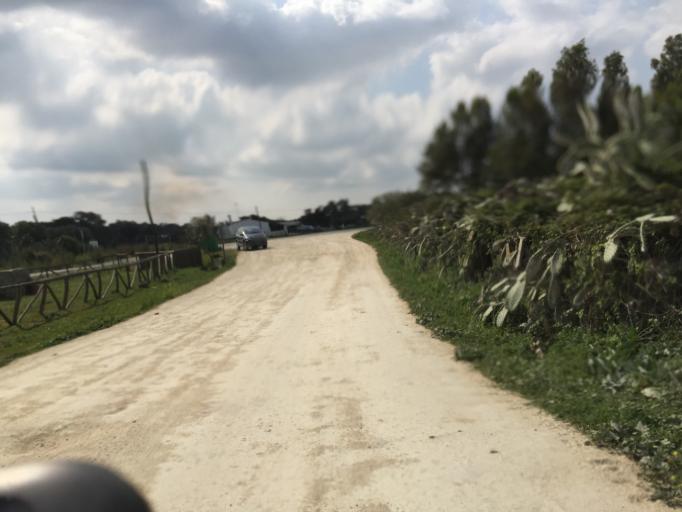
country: ES
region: Andalusia
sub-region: Provincia de Cadiz
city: Benalup-Casas Viejas
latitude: 36.3232
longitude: -5.8841
